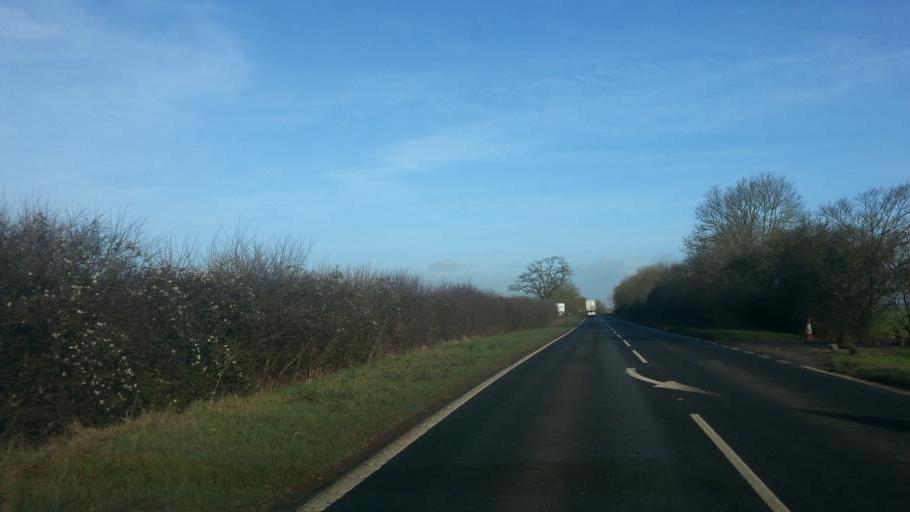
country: GB
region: England
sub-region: Cambridgeshire
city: Ramsey
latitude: 52.4187
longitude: -0.1072
